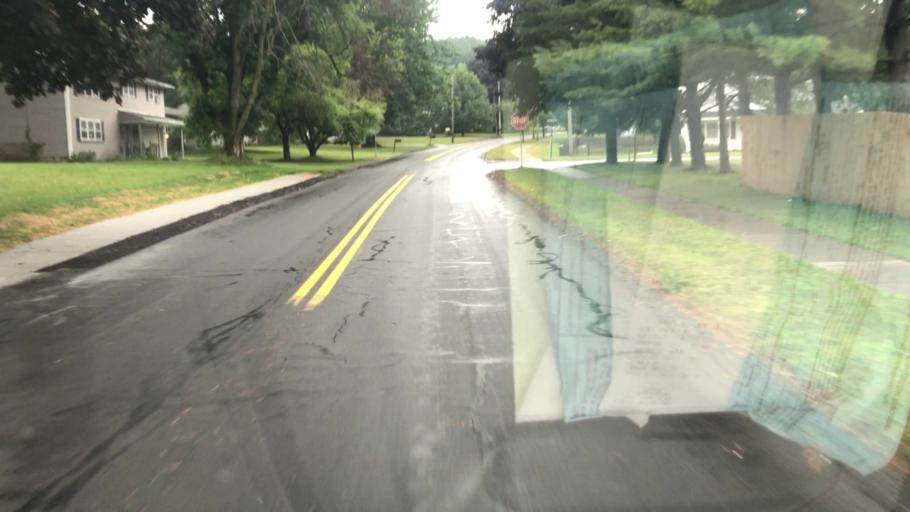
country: US
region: New York
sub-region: Onondaga County
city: Manlius
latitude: 42.9959
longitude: -75.9838
